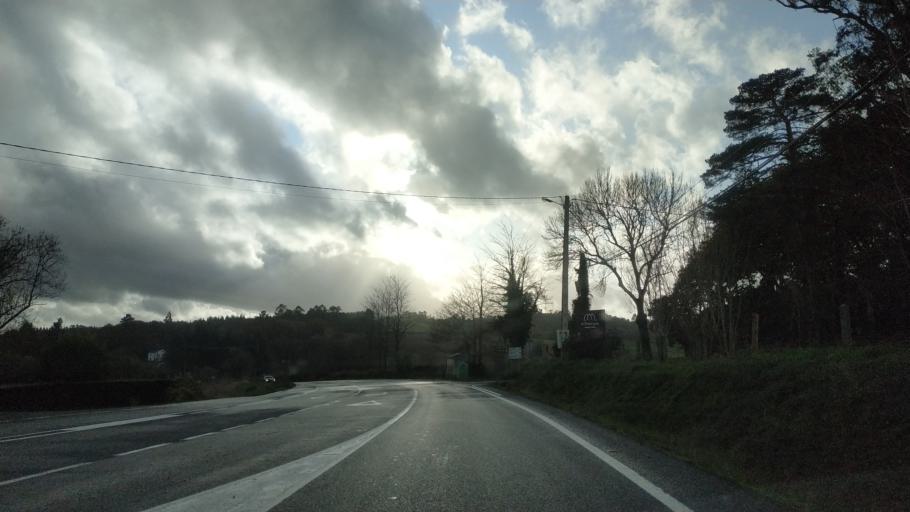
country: ES
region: Galicia
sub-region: Provincia da Coruna
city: Arzua
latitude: 42.9564
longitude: -8.1561
